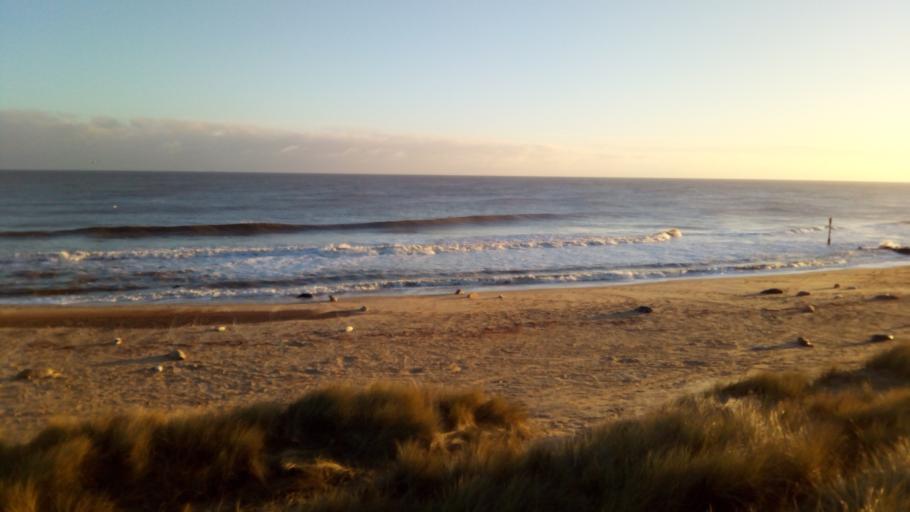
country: GB
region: England
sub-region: Norfolk
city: Martham
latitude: 52.7477
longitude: 1.6673
